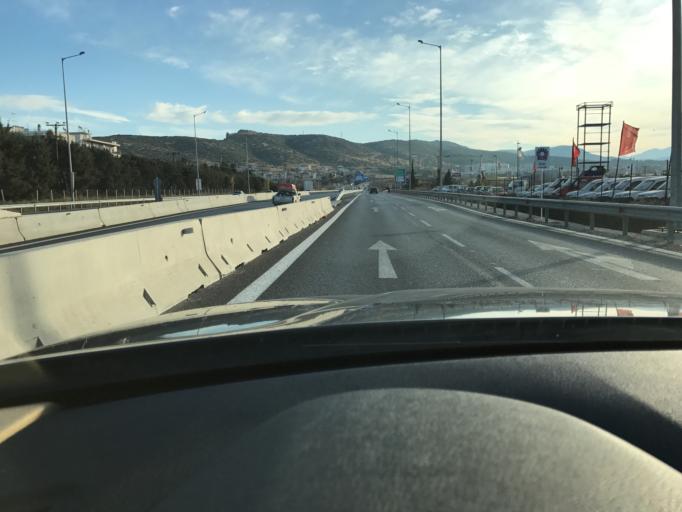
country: GR
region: Central Macedonia
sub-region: Nomos Thessalonikis
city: Efkarpia
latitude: 40.6800
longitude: 22.9494
